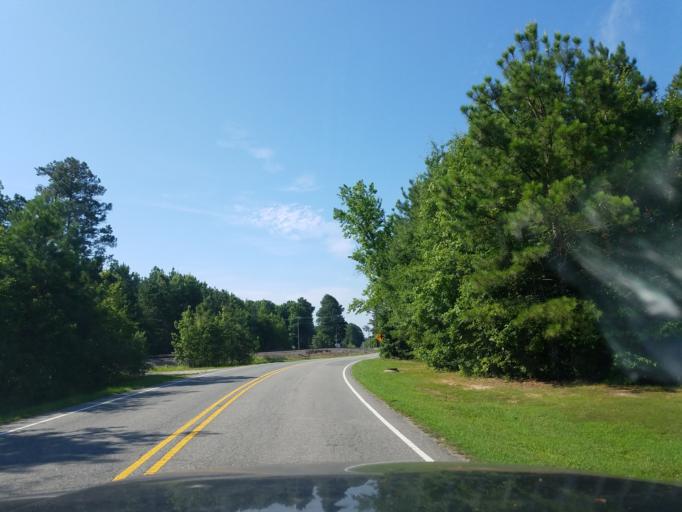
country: US
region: North Carolina
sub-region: Durham County
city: Gorman
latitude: 36.0258
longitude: -78.8410
